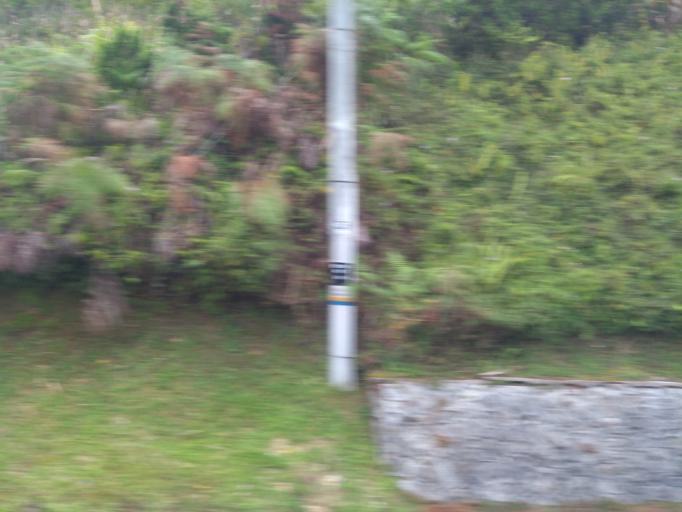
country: MY
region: Pahang
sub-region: Cameron Highlands
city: Tanah Rata
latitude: 4.4887
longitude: 101.3860
